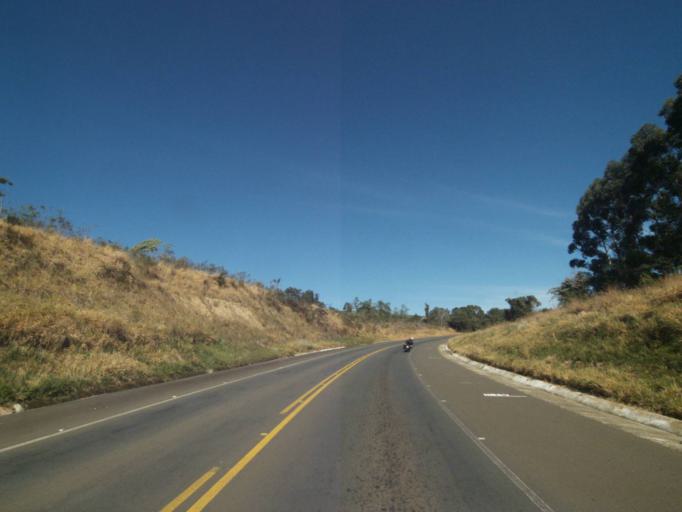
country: BR
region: Parana
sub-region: Tibagi
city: Tibagi
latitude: -24.7530
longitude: -50.4662
